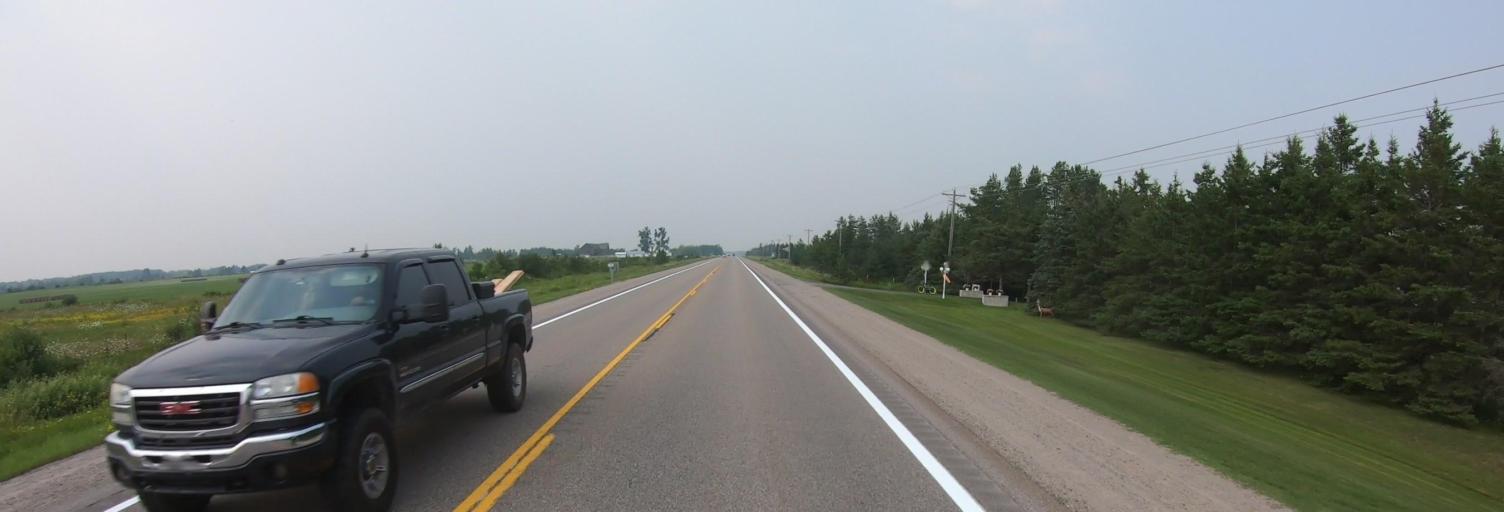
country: US
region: Michigan
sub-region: Chippewa County
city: Sault Ste. Marie
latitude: 46.3384
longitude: -84.3638
